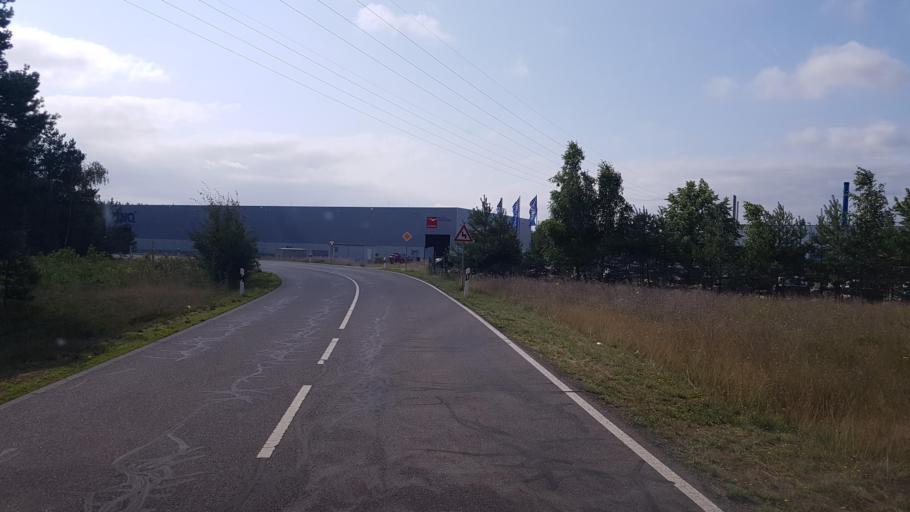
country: DE
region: Brandenburg
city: Grossraschen
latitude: 51.5945
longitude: 14.0255
